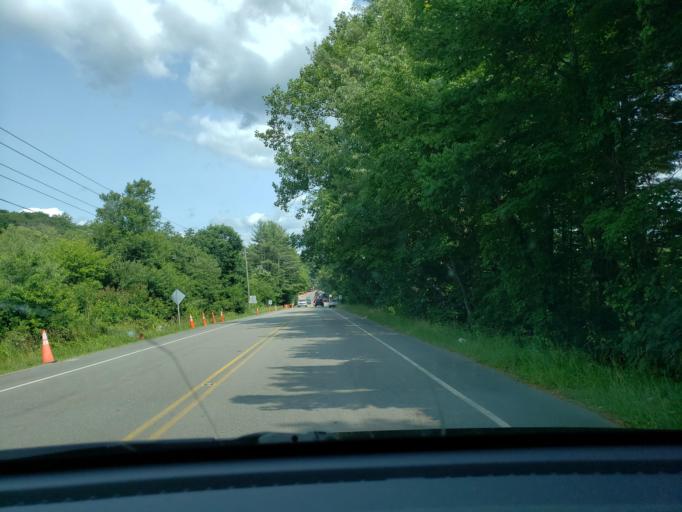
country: US
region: North Carolina
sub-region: Watauga County
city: Blowing Rock
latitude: 36.1362
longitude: -81.6827
